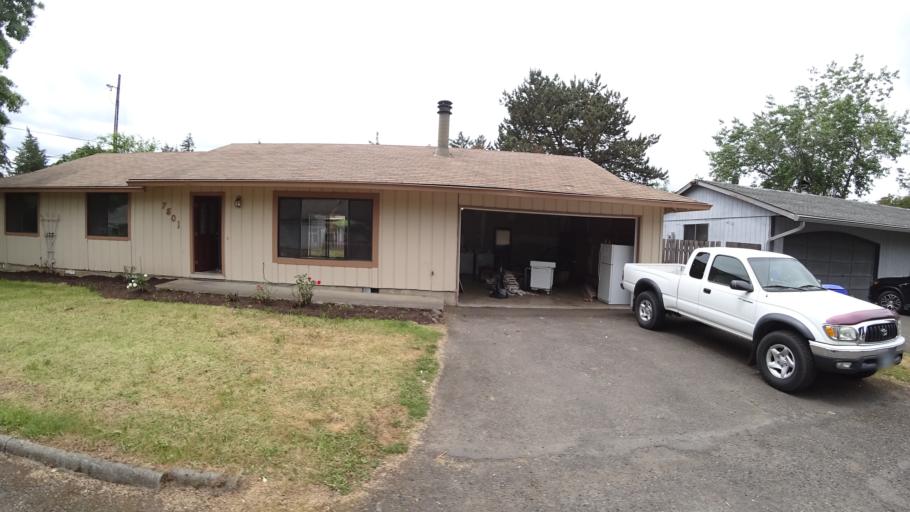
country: US
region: Oregon
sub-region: Multnomah County
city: Lents
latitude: 45.4654
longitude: -122.5832
